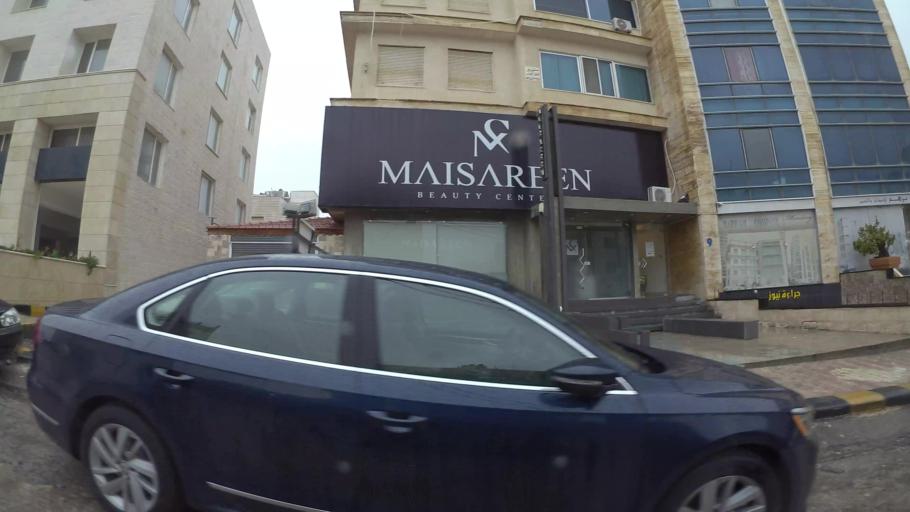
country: JO
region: Amman
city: Wadi as Sir
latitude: 31.9648
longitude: 35.8682
